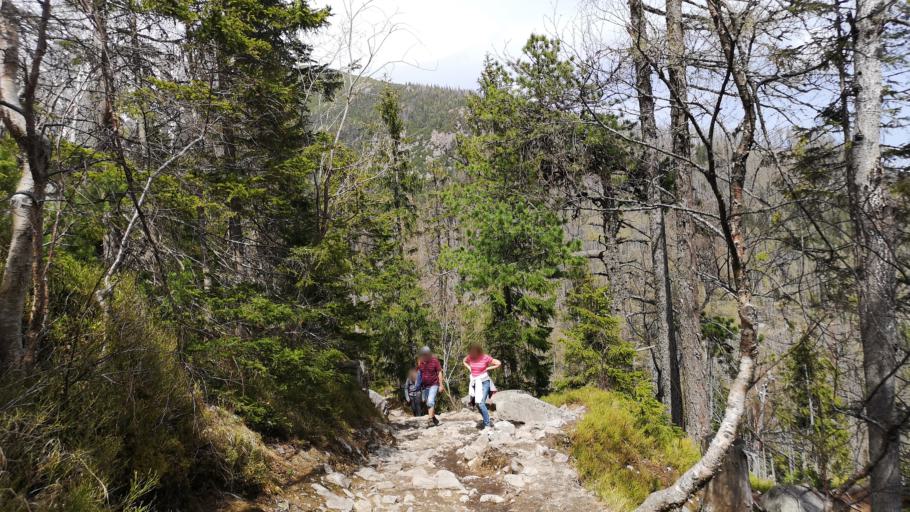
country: SK
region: Presovsky
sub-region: Okres Poprad
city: Vysoke Tatry
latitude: 49.1617
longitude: 20.2234
